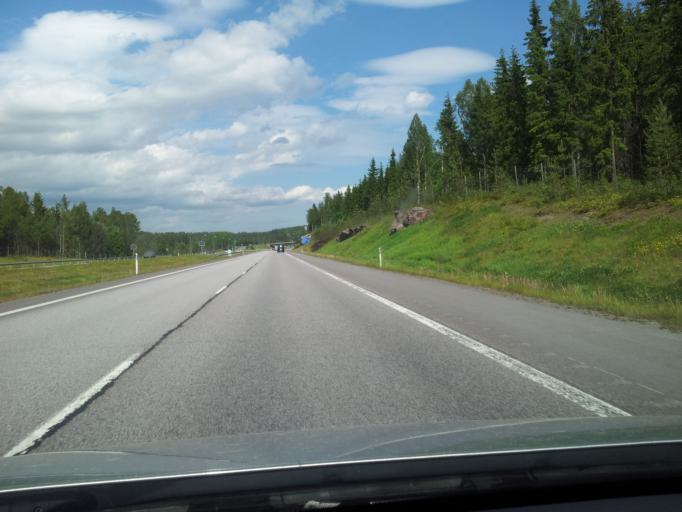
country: FI
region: Uusimaa
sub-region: Loviisa
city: Perna
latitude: 60.4822
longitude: 25.8808
